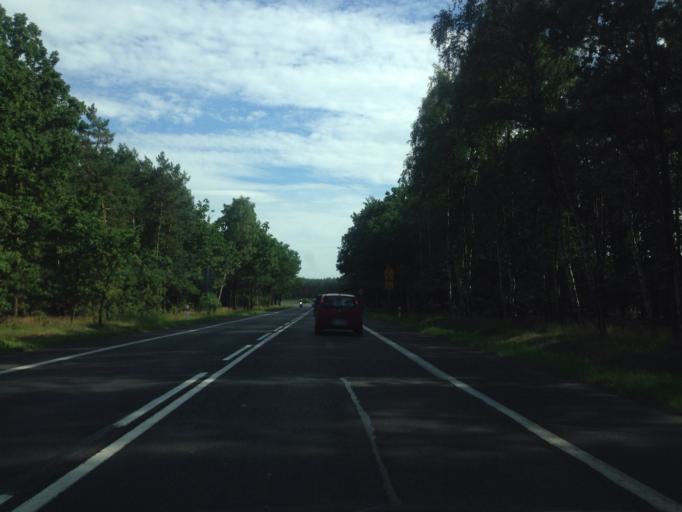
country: PL
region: Kujawsko-Pomorskie
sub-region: Powiat aleksandrowski
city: Aleksandrow Kujawski
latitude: 52.8903
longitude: 18.7321
